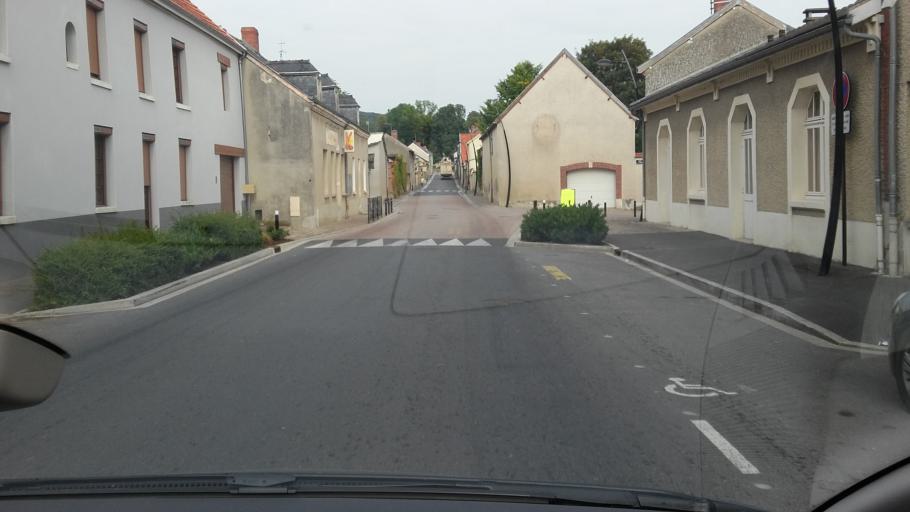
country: FR
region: Champagne-Ardenne
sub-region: Departement de la Marne
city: Tours-sur-Marne
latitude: 49.1012
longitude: 4.1141
